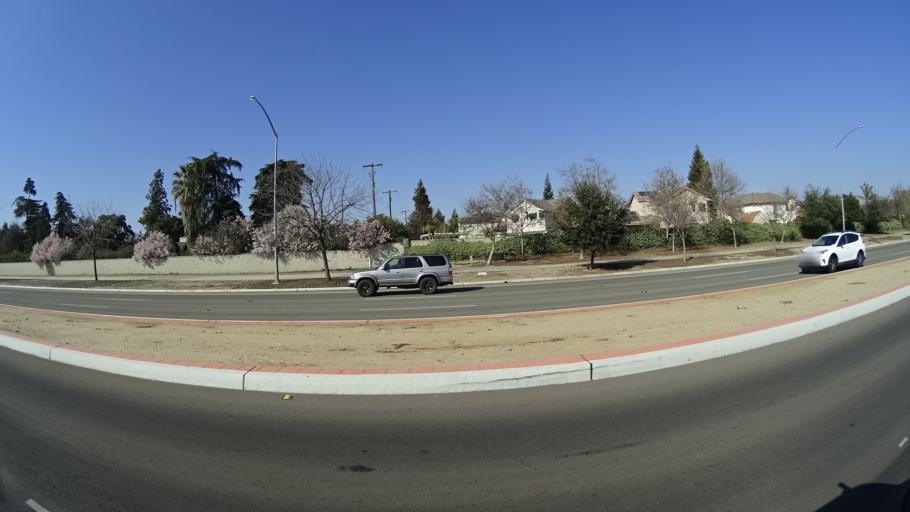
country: US
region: California
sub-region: Fresno County
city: Clovis
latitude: 36.8722
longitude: -119.7296
